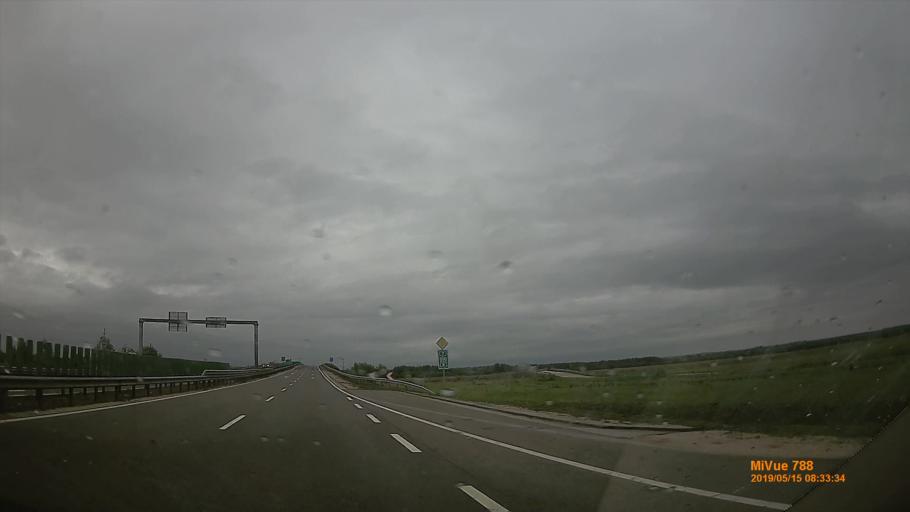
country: HU
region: Fejer
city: Szekesfehervar
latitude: 47.1769
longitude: 18.3799
